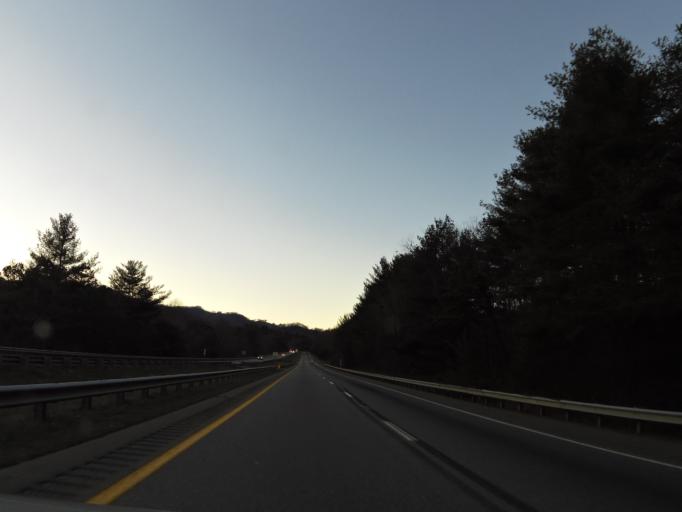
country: US
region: North Carolina
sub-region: Haywood County
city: Clyde
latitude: 35.5493
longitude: -82.9367
